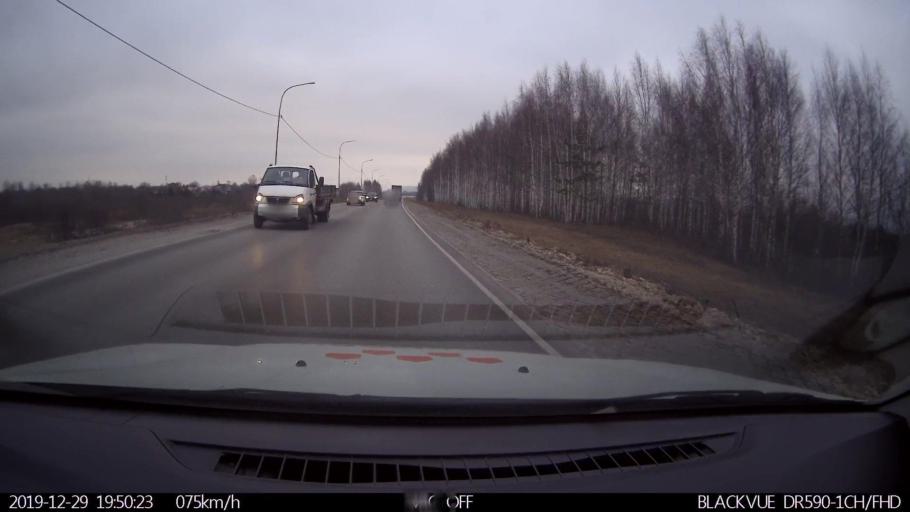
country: RU
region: Nizjnij Novgorod
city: Nizhniy Novgorod
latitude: 56.3688
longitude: 44.0276
